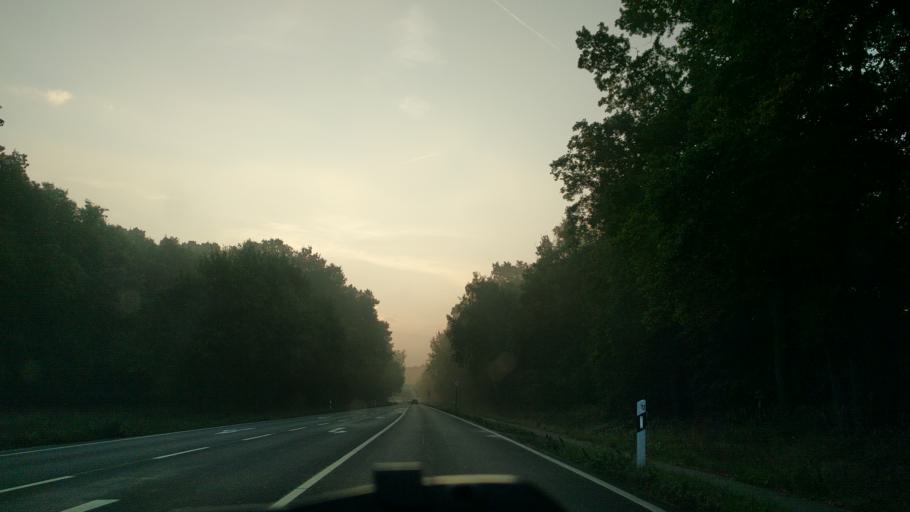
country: DE
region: Lower Saxony
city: Isenbuttel
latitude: 52.4396
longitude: 10.6039
